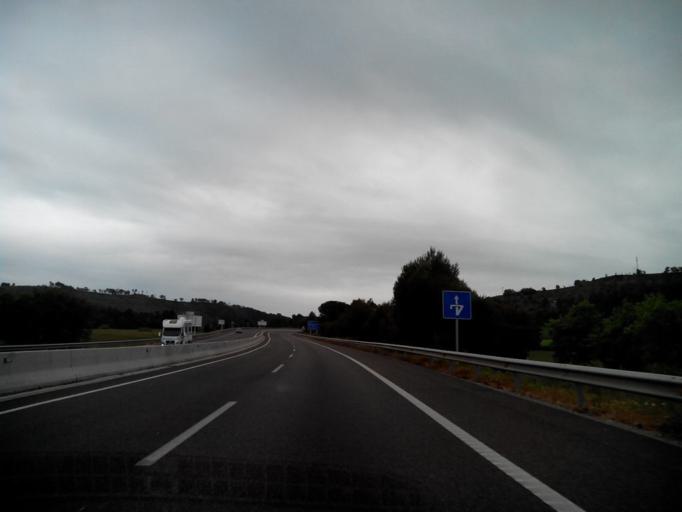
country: ES
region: Catalonia
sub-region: Provincia de Barcelona
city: Calaf
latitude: 41.7413
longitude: 1.5712
